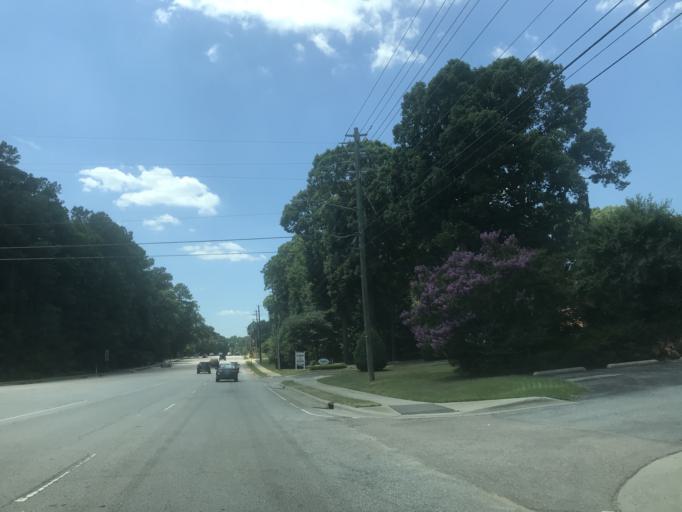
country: US
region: North Carolina
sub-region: Wake County
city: Cary
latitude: 35.7643
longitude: -78.7495
